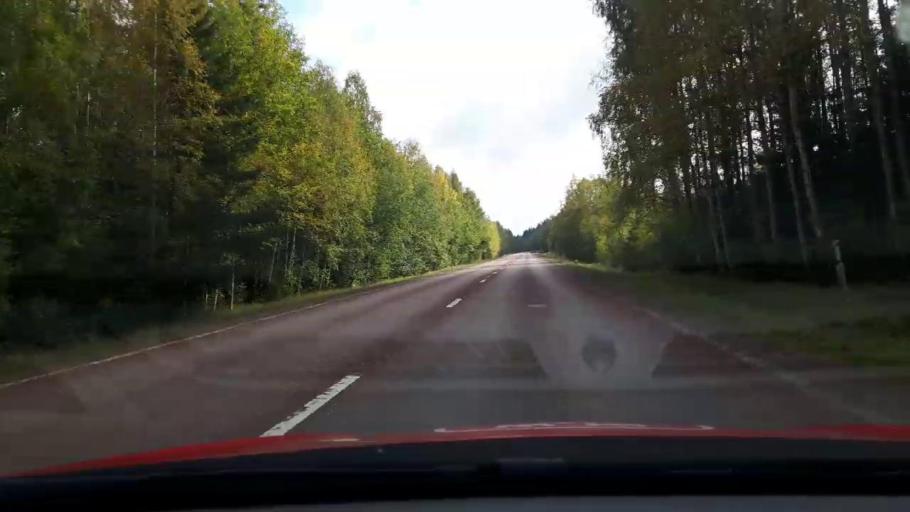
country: SE
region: Gaevleborg
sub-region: Ljusdals Kommun
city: Jaervsoe
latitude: 61.6424
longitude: 16.2273
